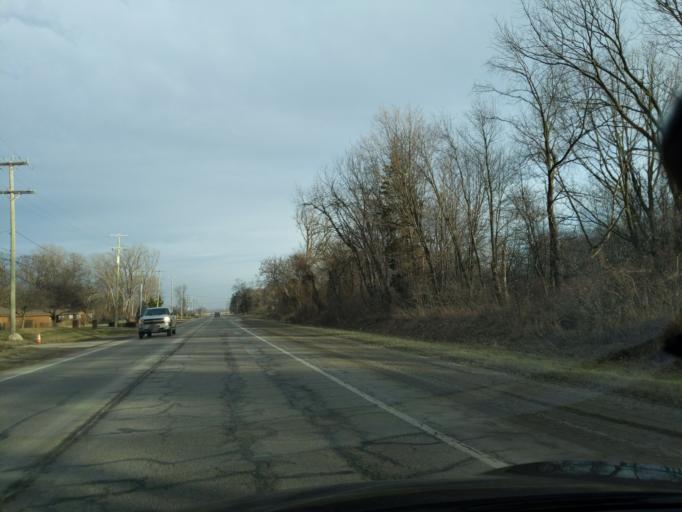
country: US
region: Michigan
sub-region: Livingston County
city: Fowlerville
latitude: 42.6608
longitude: -84.0465
